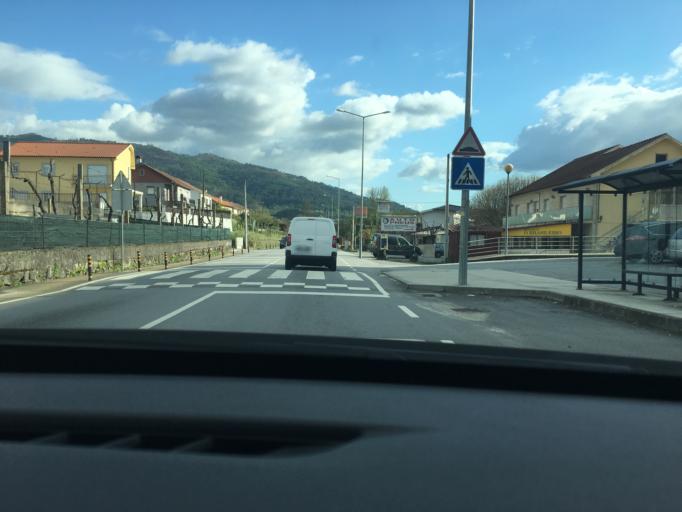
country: PT
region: Viana do Castelo
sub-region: Ponte da Barca
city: Ponte da Barca
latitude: 41.7964
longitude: -8.4145
